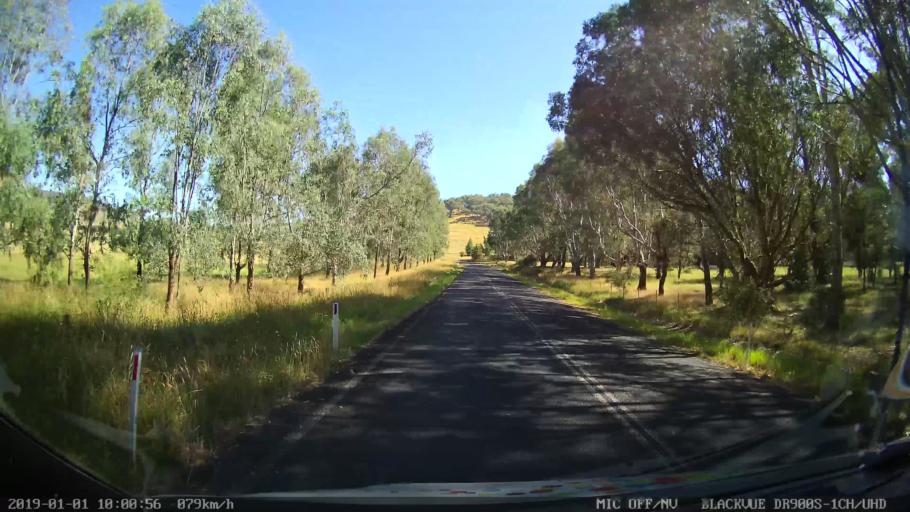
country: AU
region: New South Wales
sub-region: Snowy River
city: Jindabyne
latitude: -36.1967
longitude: 148.1029
